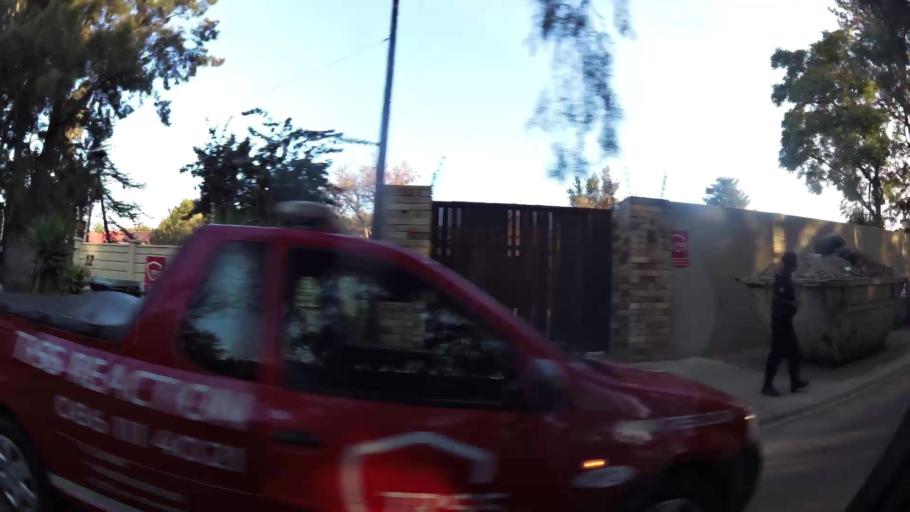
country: ZA
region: Gauteng
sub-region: City of Johannesburg Metropolitan Municipality
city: Diepsloot
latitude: -26.0504
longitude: 27.9760
